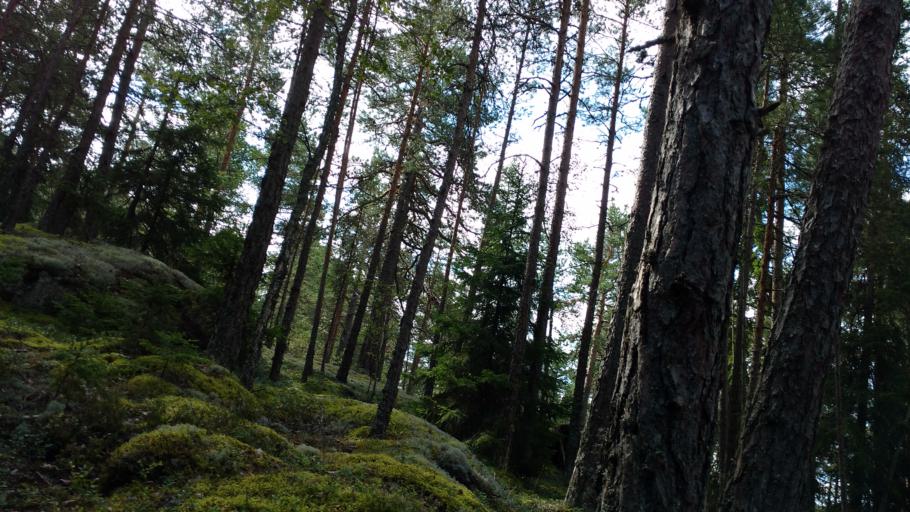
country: FI
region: Varsinais-Suomi
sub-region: Salo
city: Salo
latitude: 60.3674
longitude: 23.1784
